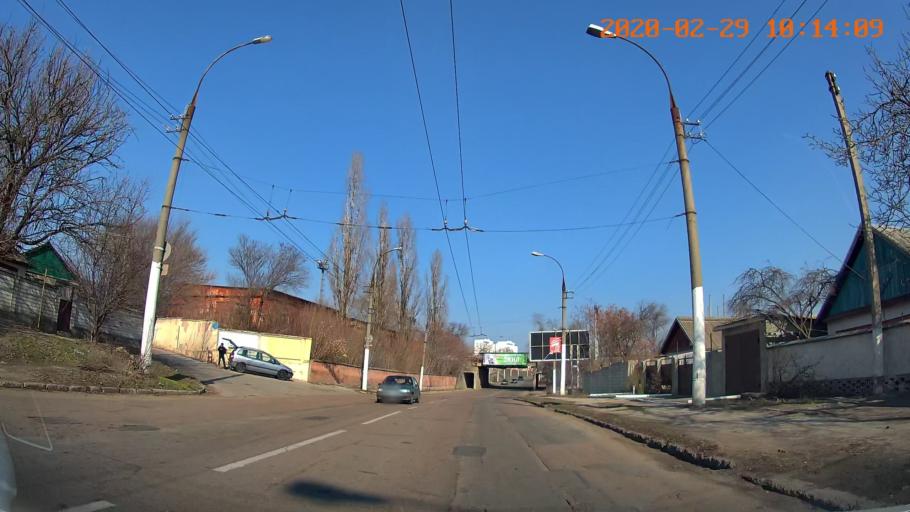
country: MD
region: Telenesti
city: Tiraspolul Nou
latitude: 46.8442
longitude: 29.6443
